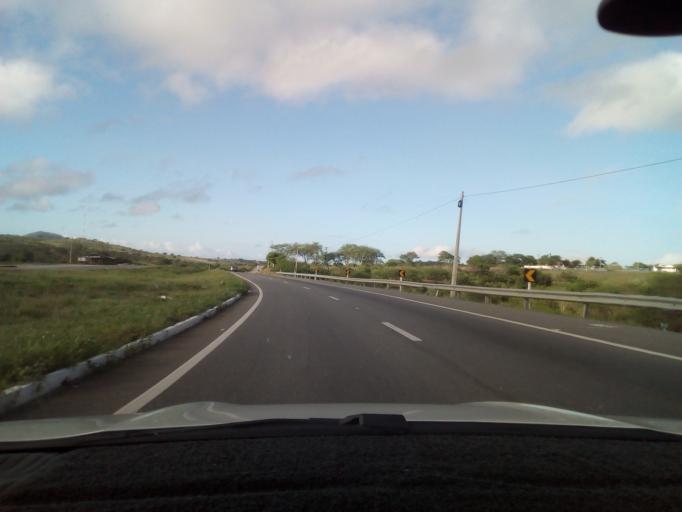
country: BR
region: Paraiba
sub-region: Inga
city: Inga
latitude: -7.2176
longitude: -35.5957
